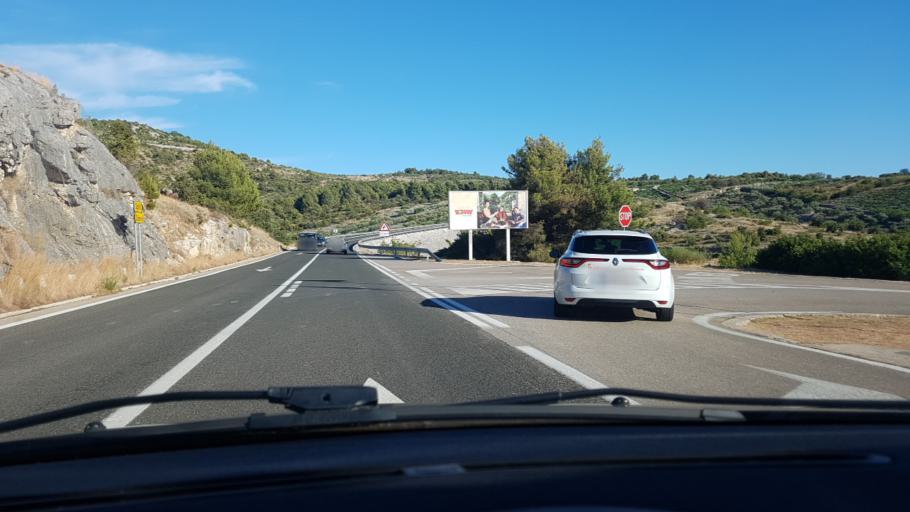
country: HR
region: Sibensko-Kniniska
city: Primosten
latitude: 43.5700
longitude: 15.9453
